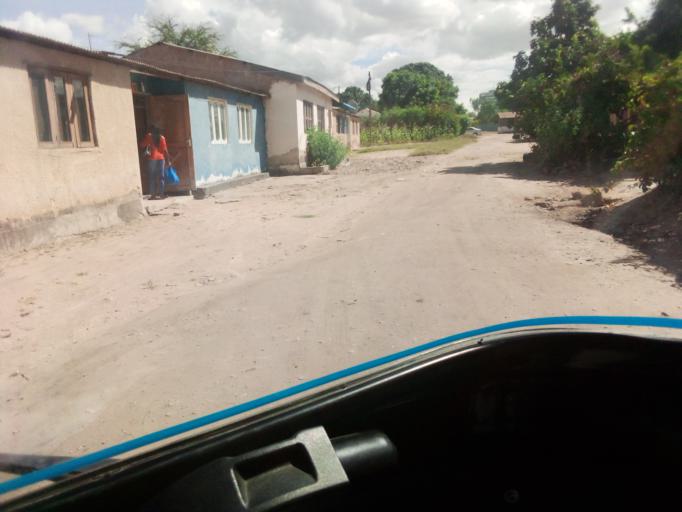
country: TZ
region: Dodoma
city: Dodoma
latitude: -6.1777
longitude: 35.7569
